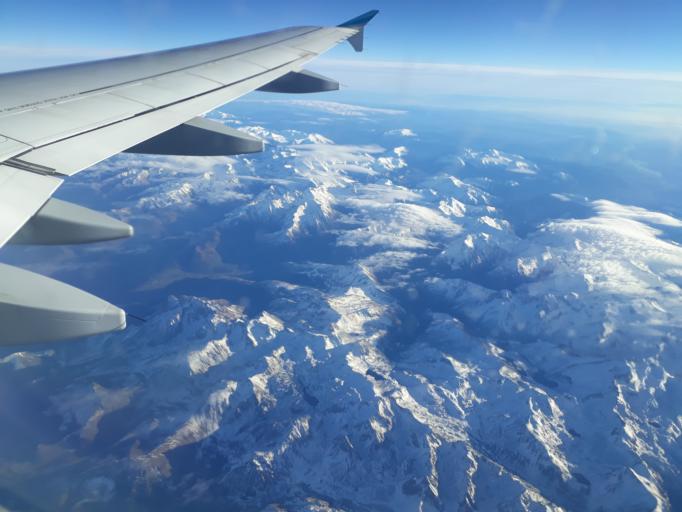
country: FR
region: Midi-Pyrenees
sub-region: Departement des Hautes-Pyrenees
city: Campan
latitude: 42.9830
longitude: 0.1068
